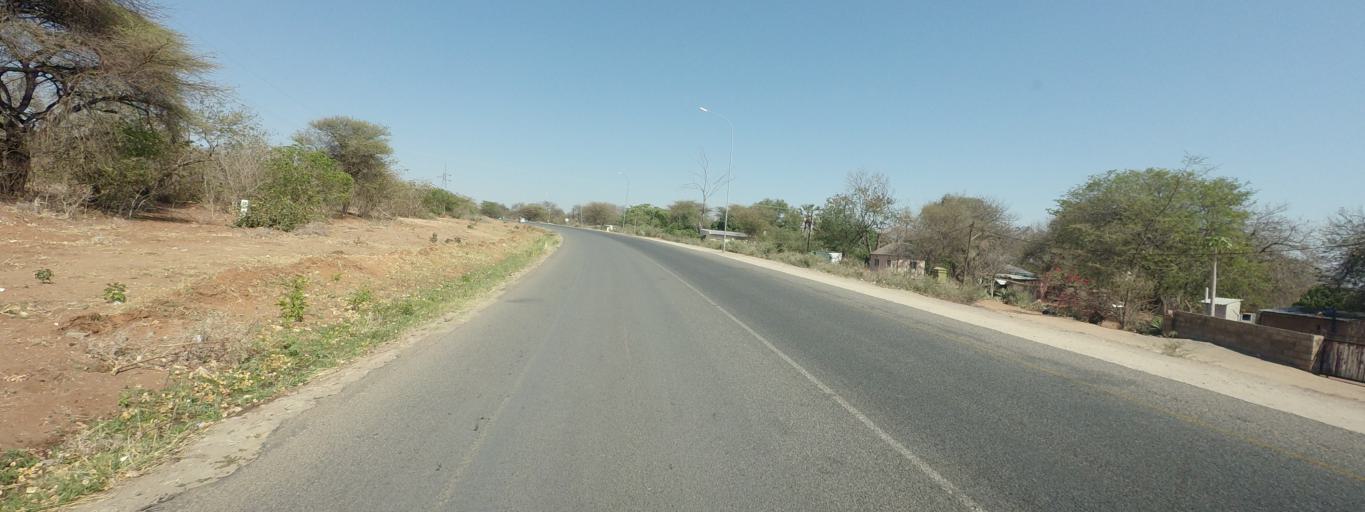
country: BW
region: North West
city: Kasane
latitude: -17.7990
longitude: 25.2362
